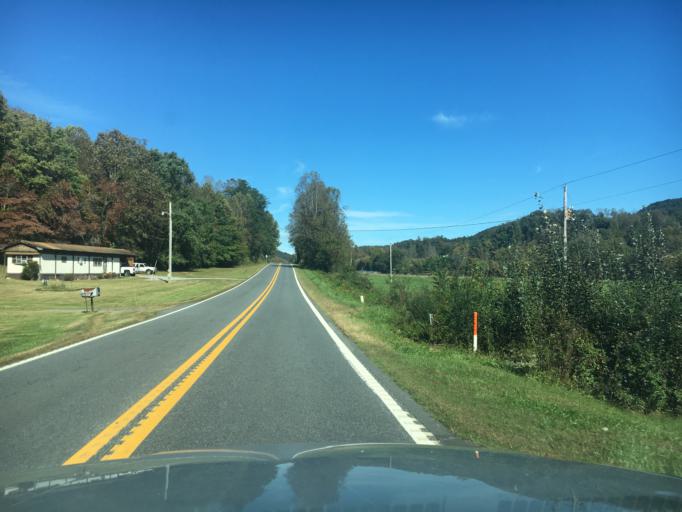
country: US
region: North Carolina
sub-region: Rutherford County
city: Spindale
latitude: 35.5218
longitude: -81.8551
